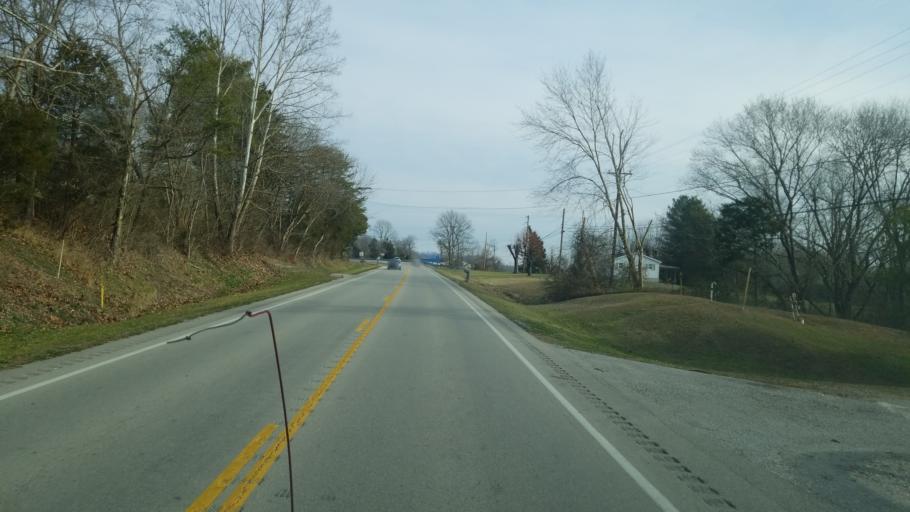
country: US
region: Kentucky
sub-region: Casey County
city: Liberty
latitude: 37.3305
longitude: -84.9108
